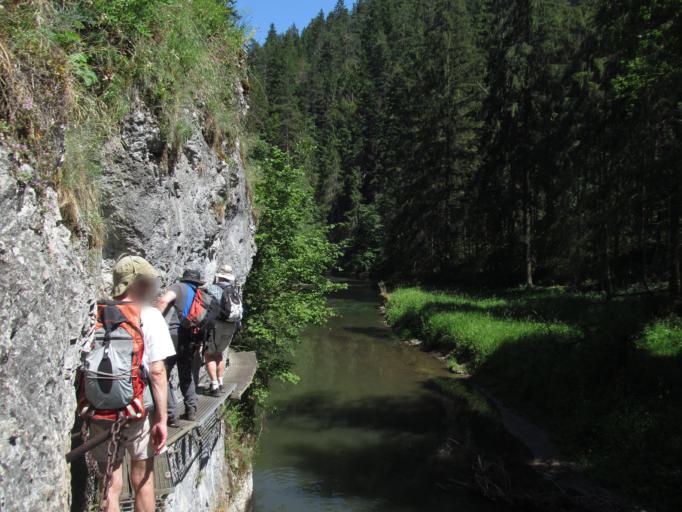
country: SK
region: Kosicky
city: Dobsina
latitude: 48.9568
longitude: 20.4095
